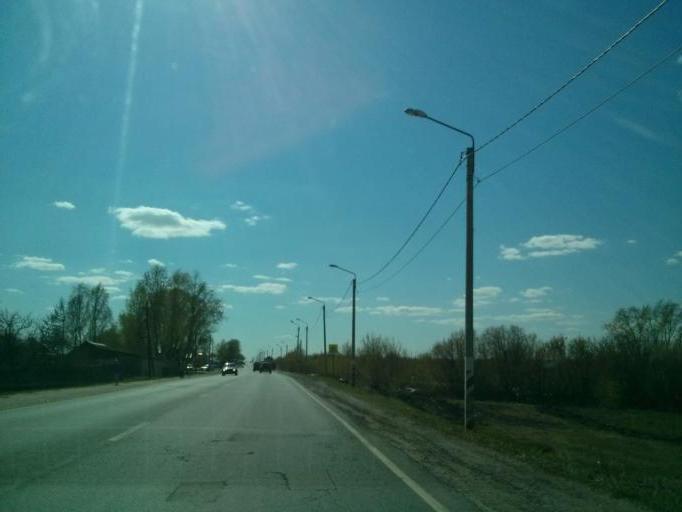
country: RU
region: Nizjnij Novgorod
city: Pavlovo
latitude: 55.9514
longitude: 43.1160
